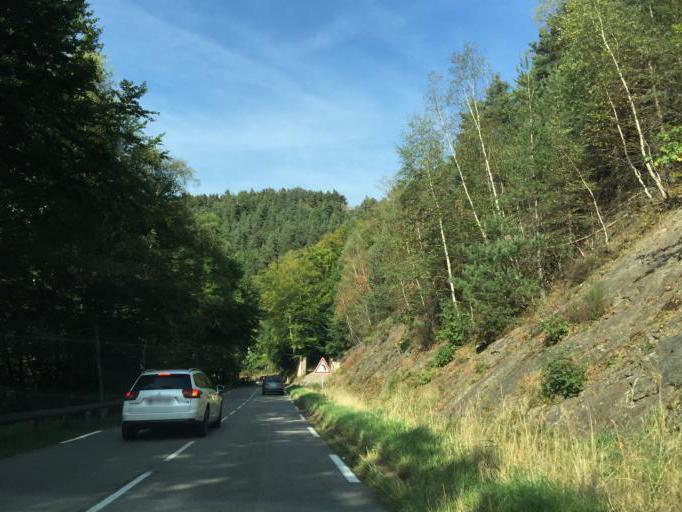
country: FR
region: Rhone-Alpes
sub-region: Departement de la Loire
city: Saint-Jean-Bonnefonds
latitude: 45.4007
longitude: 4.4513
